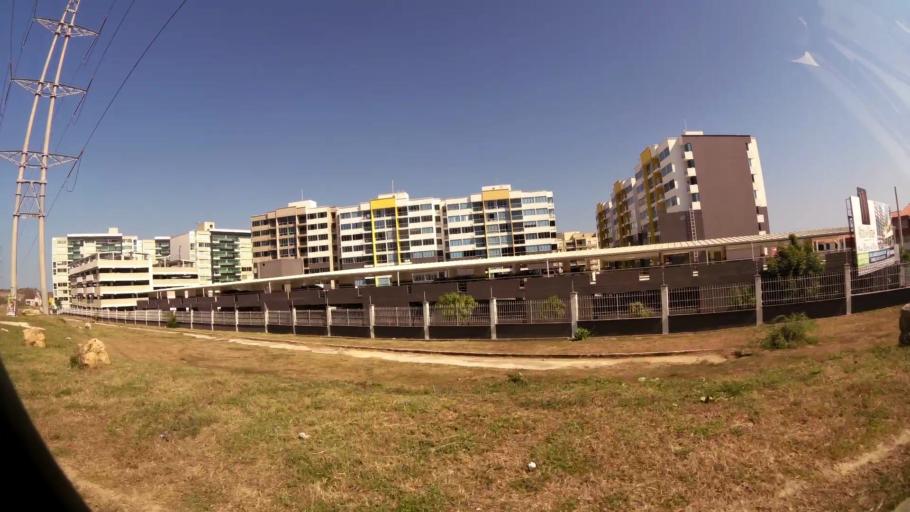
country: CO
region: Atlantico
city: Barranquilla
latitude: 11.0189
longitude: -74.8181
